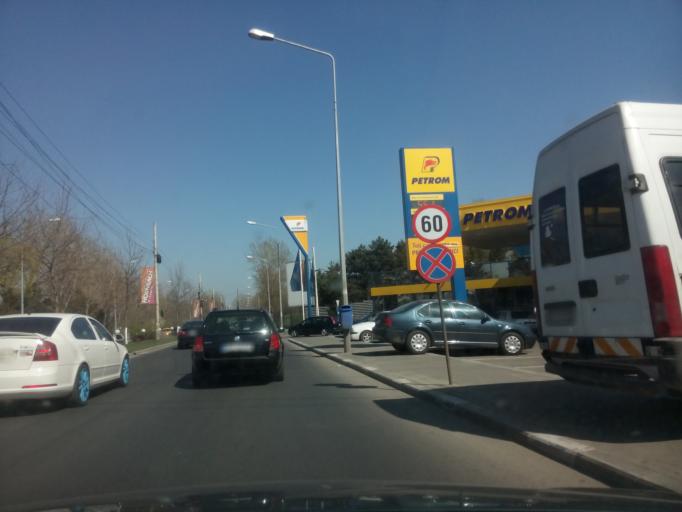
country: RO
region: Ilfov
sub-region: Comuna Pantelimon
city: Pantelimon
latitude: 44.4411
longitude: 26.1919
